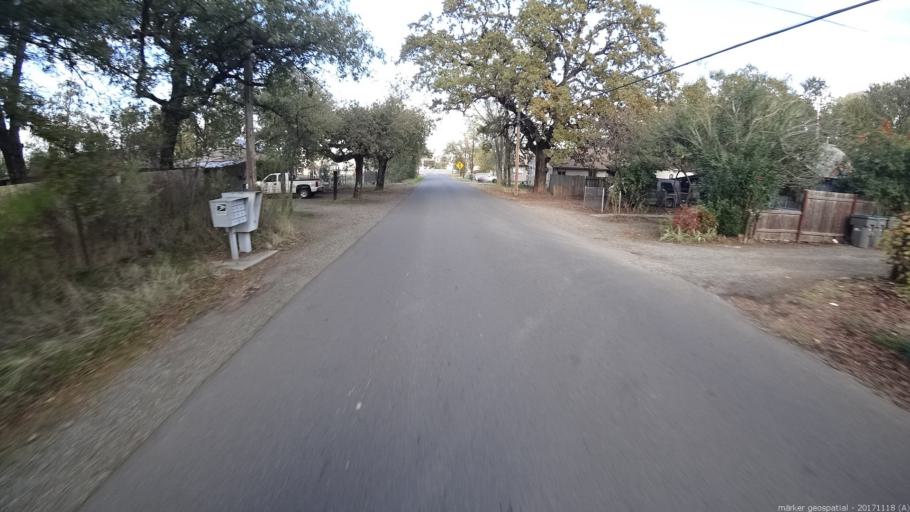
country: US
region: California
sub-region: Shasta County
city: Anderson
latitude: 40.4583
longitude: -122.3166
